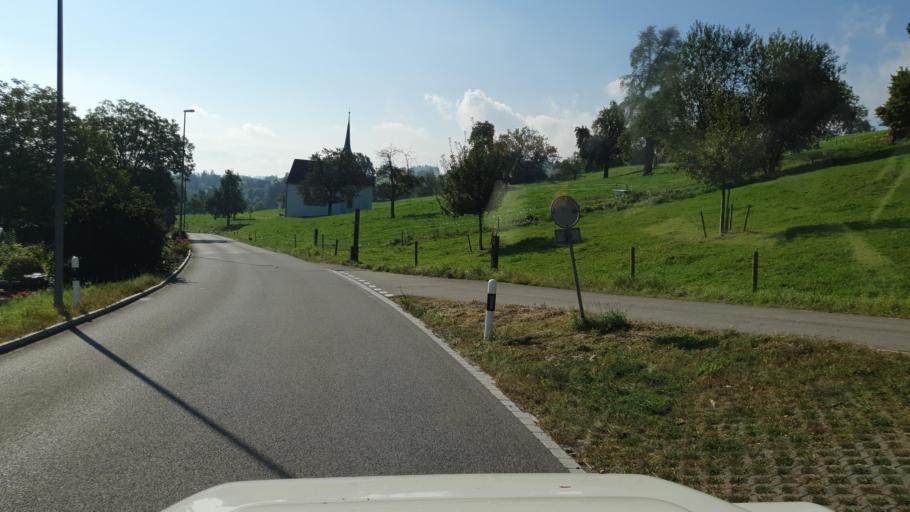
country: CH
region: Aargau
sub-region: Bezirk Muri
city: Waltenschwil
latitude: 47.3027
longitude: 8.3041
